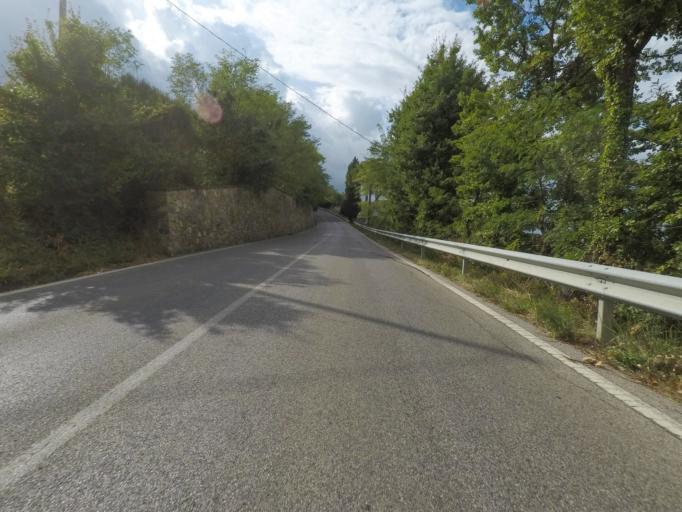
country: IT
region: Tuscany
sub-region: Provincia di Siena
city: Montepulciano
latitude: 43.1132
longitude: 11.7894
